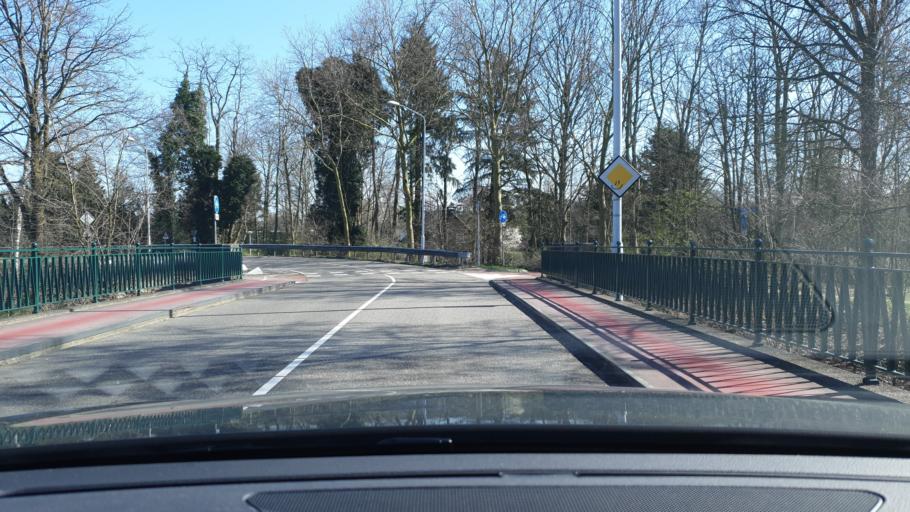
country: NL
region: North Brabant
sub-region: Gemeente Best
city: Best
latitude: 51.4910
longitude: 5.3910
